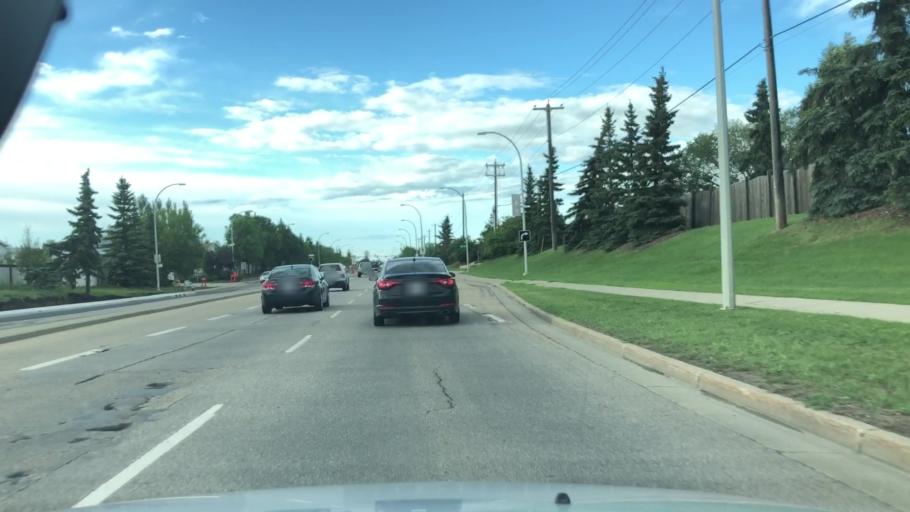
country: CA
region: Alberta
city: St. Albert
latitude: 53.6193
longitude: -113.5411
